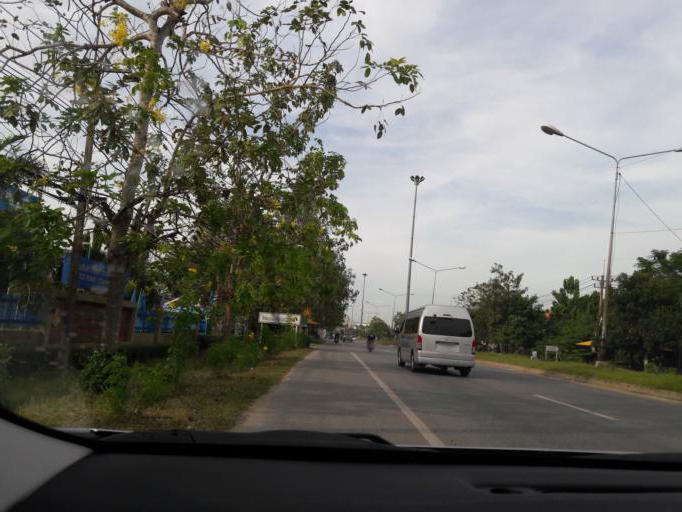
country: TH
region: Ang Thong
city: Ang Thong
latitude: 14.5791
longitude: 100.4531
